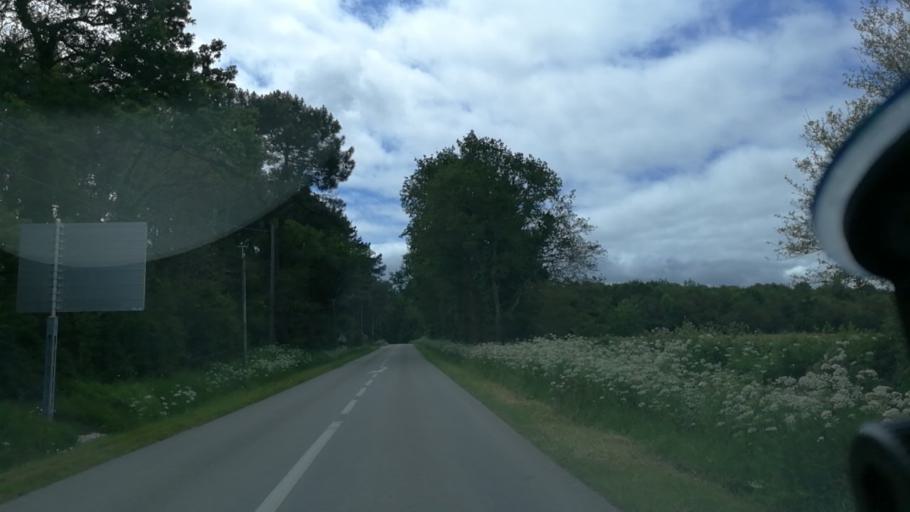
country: FR
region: Brittany
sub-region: Departement du Morbihan
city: Penestin
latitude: 47.4777
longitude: -2.4342
